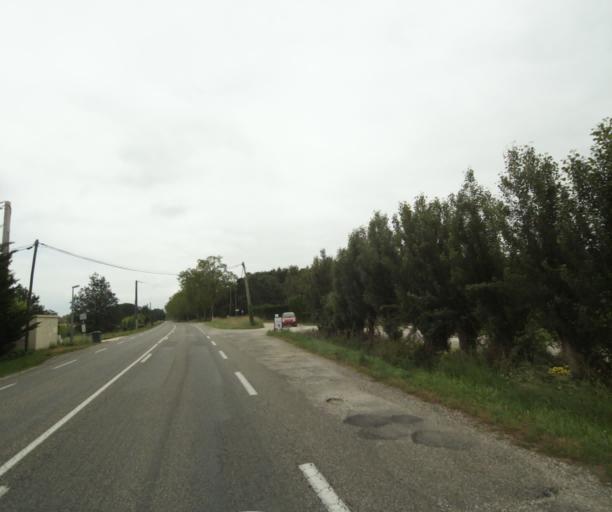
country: FR
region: Midi-Pyrenees
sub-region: Departement du Tarn-et-Garonne
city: Saint-Nauphary
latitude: 43.9777
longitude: 1.3997
